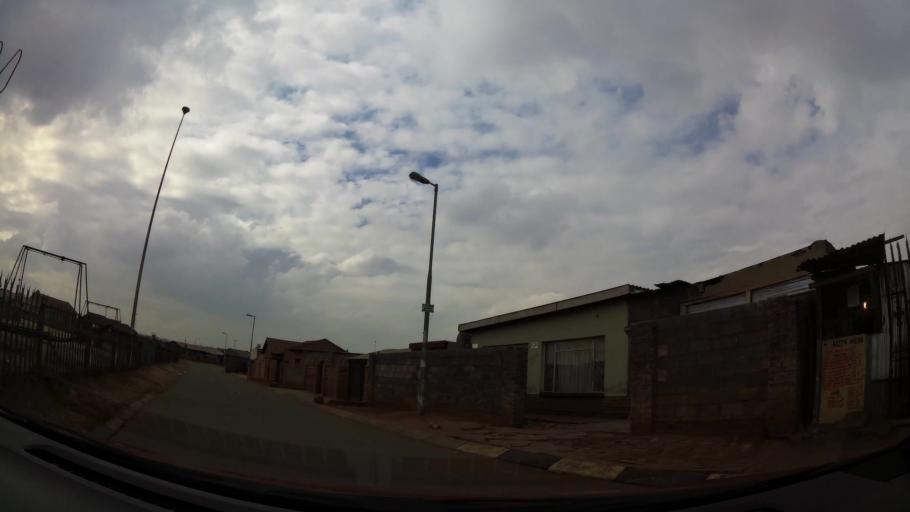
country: ZA
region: Gauteng
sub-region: City of Johannesburg Metropolitan Municipality
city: Soweto
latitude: -26.2547
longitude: 27.8270
